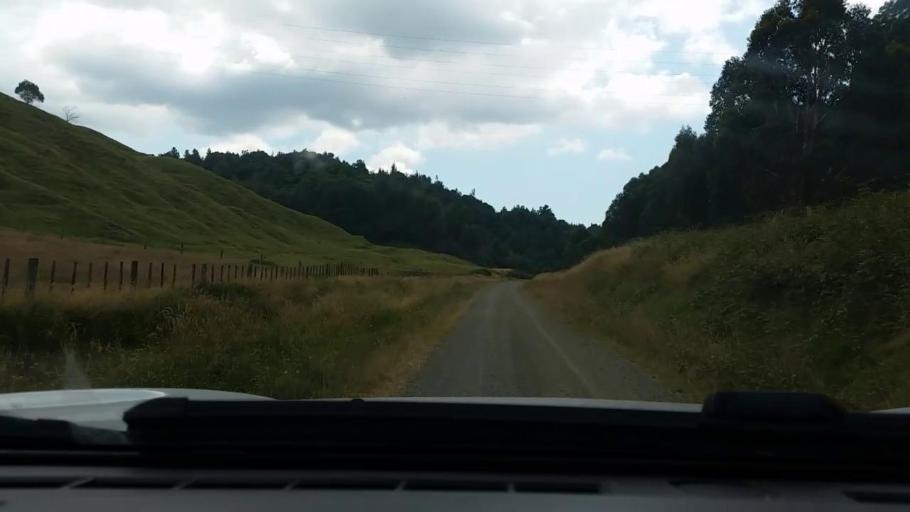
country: NZ
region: Bay of Plenty
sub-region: Kawerau District
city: Kawerau
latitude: -38.0121
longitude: 176.5973
